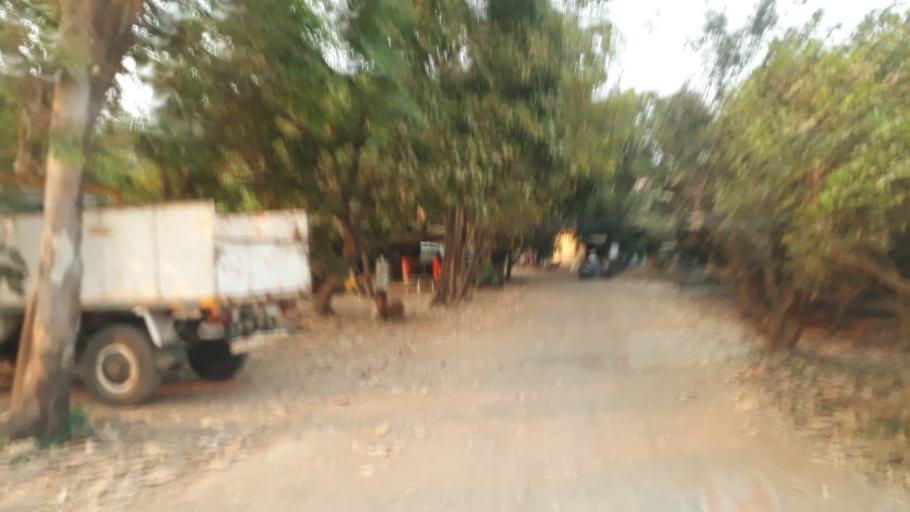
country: IN
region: Maharashtra
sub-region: Raigarh
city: Neral
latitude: 19.0426
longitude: 73.3245
